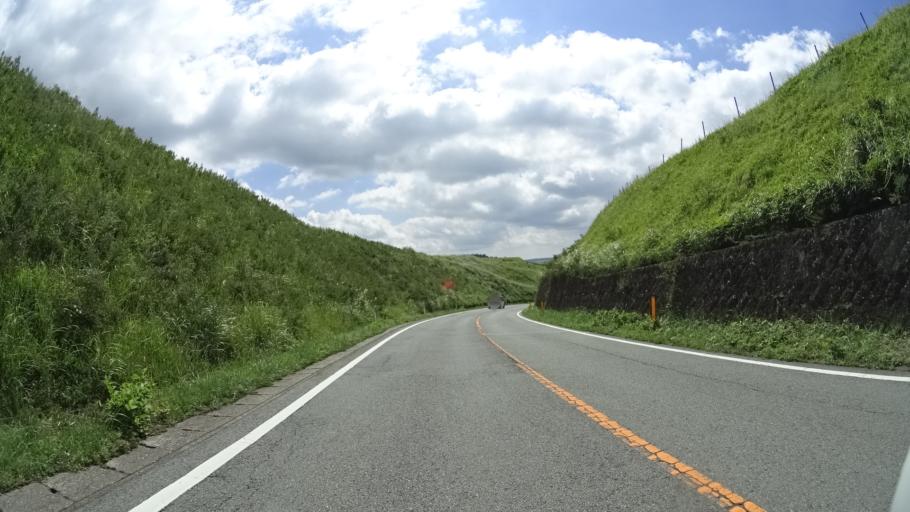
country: JP
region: Kumamoto
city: Aso
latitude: 33.0202
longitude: 131.1547
